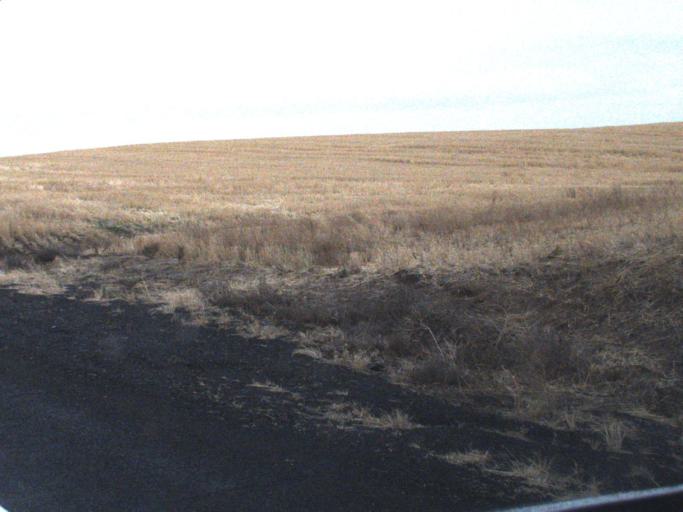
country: US
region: Washington
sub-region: Garfield County
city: Pomeroy
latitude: 46.8135
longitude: -117.8058
